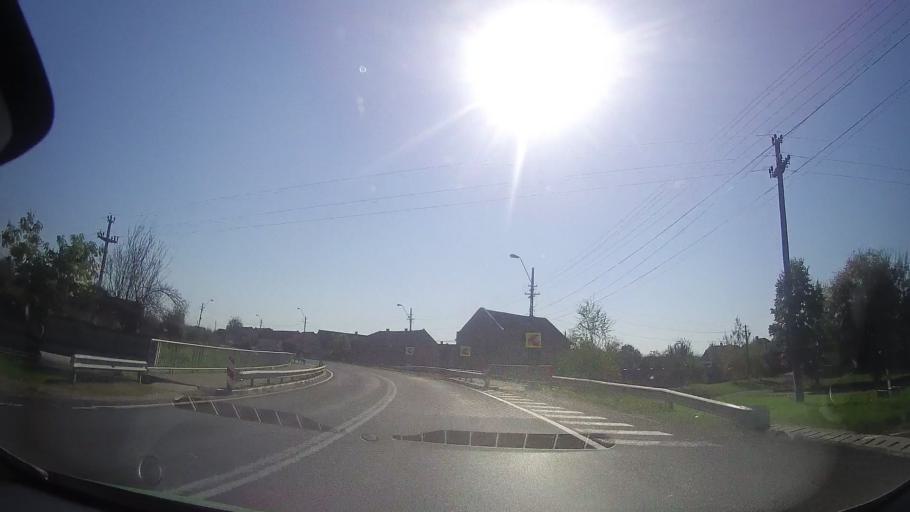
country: RO
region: Timis
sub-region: Comuna Belint
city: Belint
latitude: 45.7565
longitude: 21.7337
